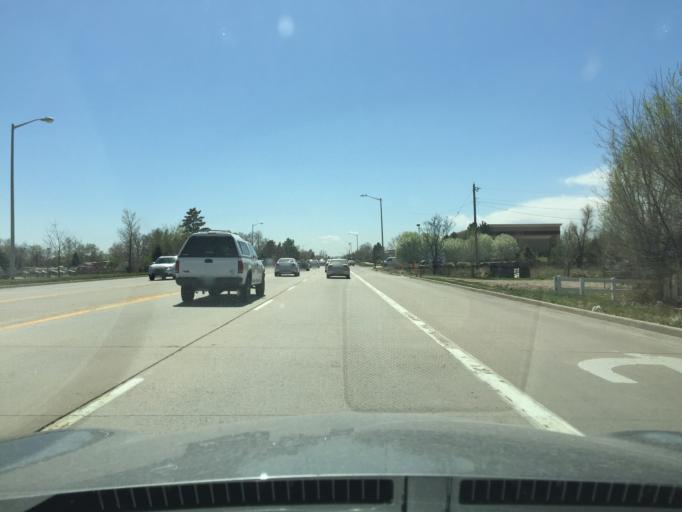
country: US
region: Colorado
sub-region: Boulder County
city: Longmont
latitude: 40.1571
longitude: -105.1308
